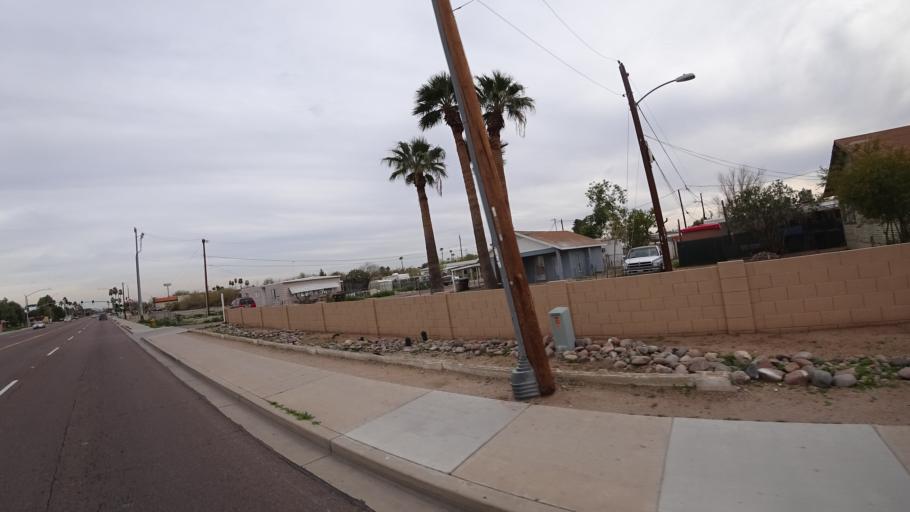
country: US
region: Arizona
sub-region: Maricopa County
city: Peoria
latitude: 33.5807
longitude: -112.2525
